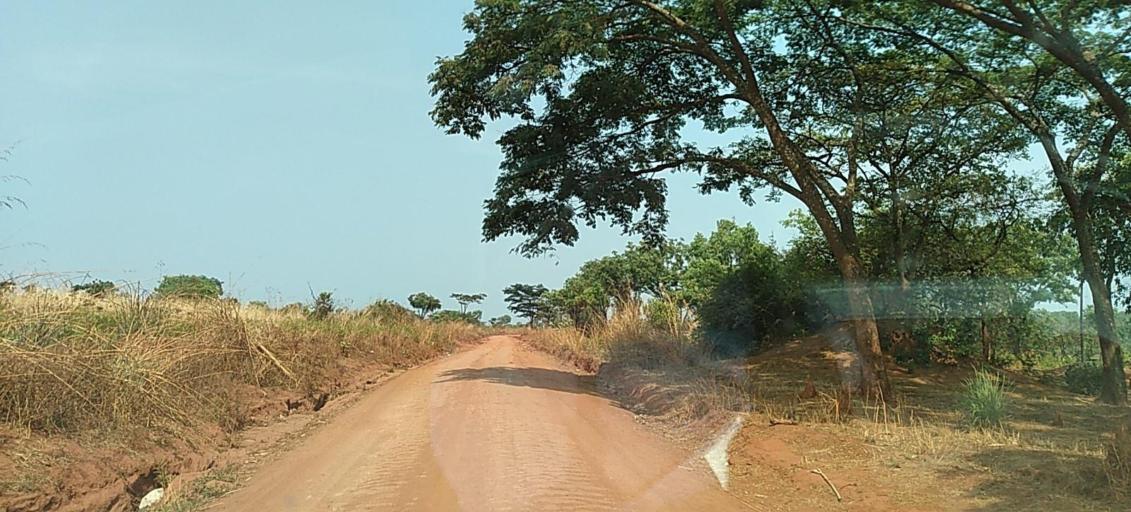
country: ZM
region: Copperbelt
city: Chililabombwe
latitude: -12.3424
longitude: 27.7038
